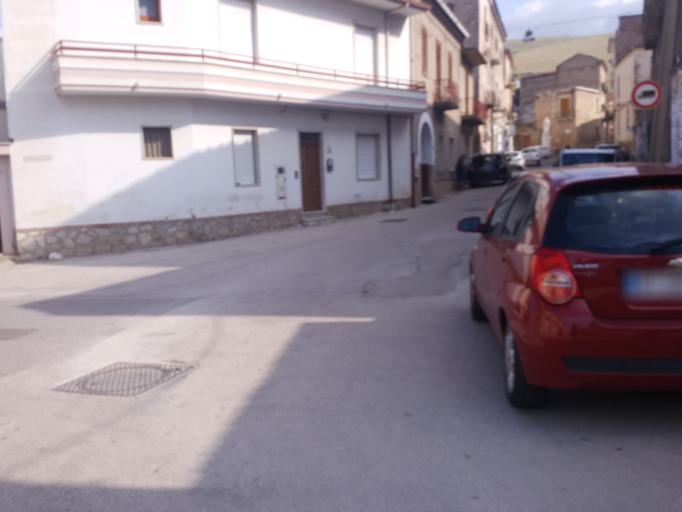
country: IT
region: Campania
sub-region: Provincia di Caserta
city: Pignataro Maggiore
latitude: 41.1897
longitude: 14.1701
